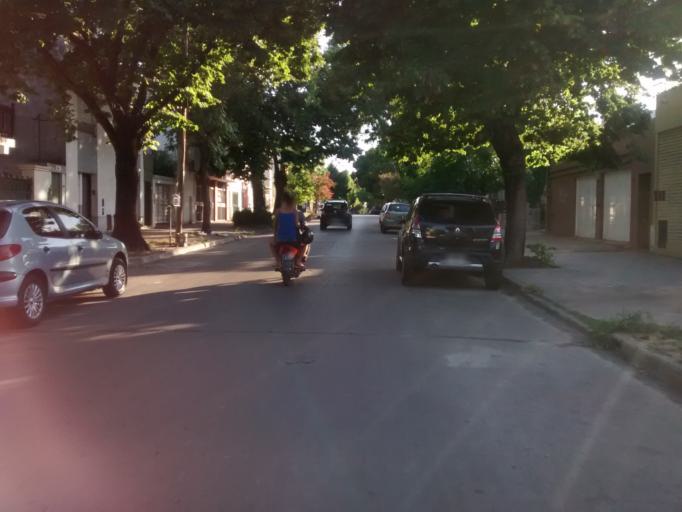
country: AR
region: Buenos Aires
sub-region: Partido de La Plata
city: La Plata
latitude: -34.9170
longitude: -57.9291
